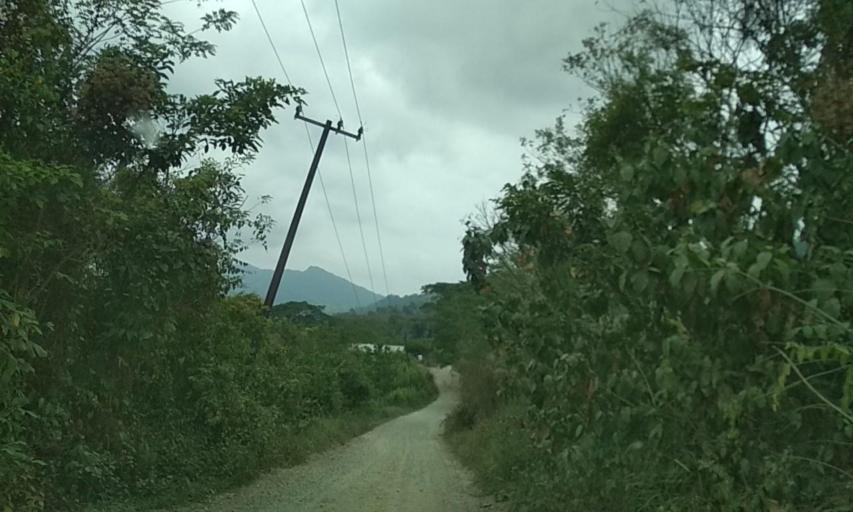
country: MX
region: Veracruz
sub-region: Uxpanapa
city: Poblado 10
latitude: 17.4937
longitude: -94.1315
